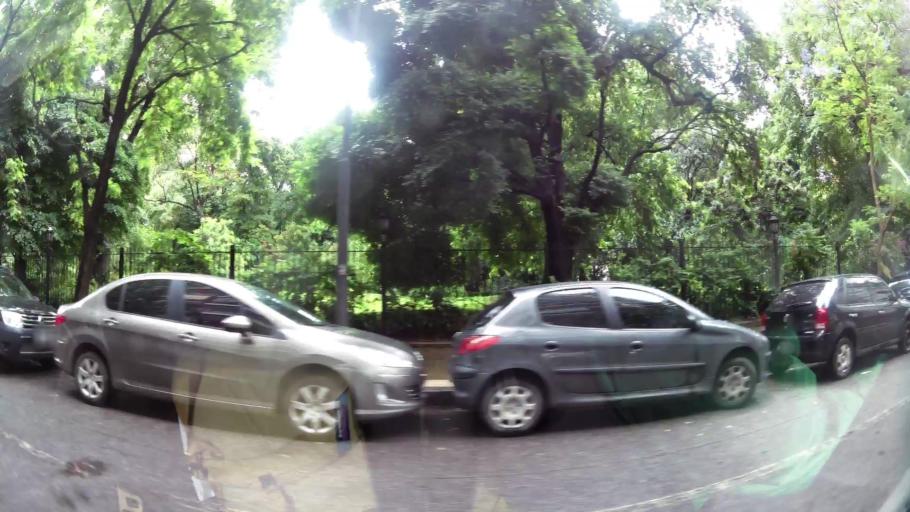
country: AR
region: Buenos Aires F.D.
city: Retiro
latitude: -34.5826
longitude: -58.4149
